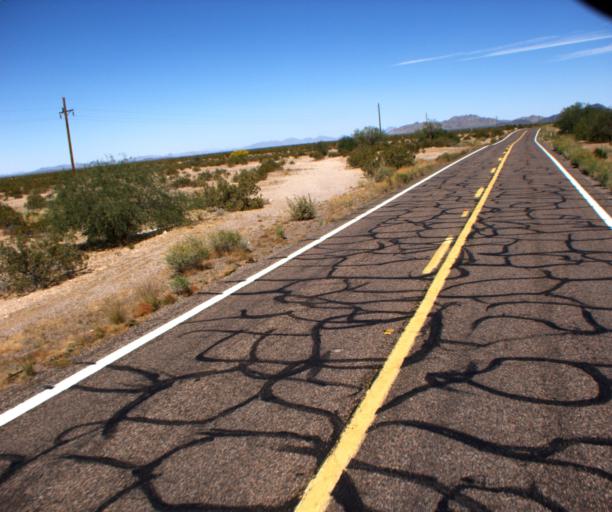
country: US
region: Arizona
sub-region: Maricopa County
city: Gila Bend
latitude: 32.6829
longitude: -112.8555
